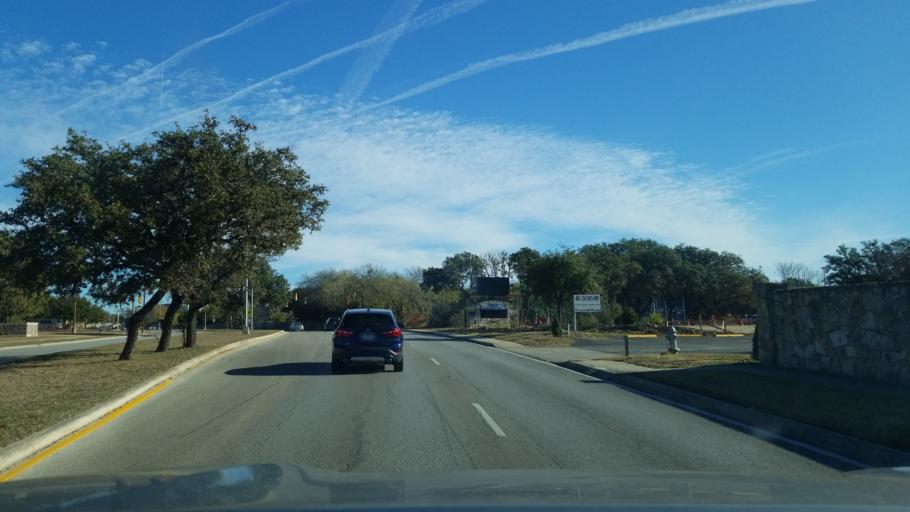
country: US
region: Texas
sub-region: Bexar County
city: Shavano Park
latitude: 29.5865
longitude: -98.5310
